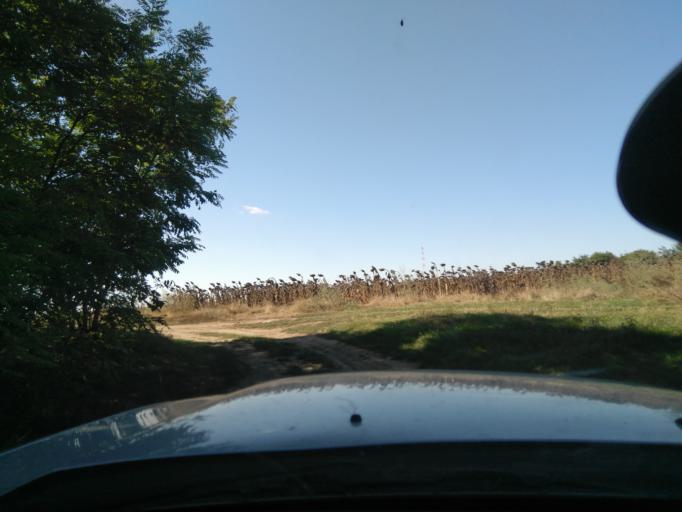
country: HU
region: Fejer
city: Pazmand
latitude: 47.3033
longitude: 18.7008
